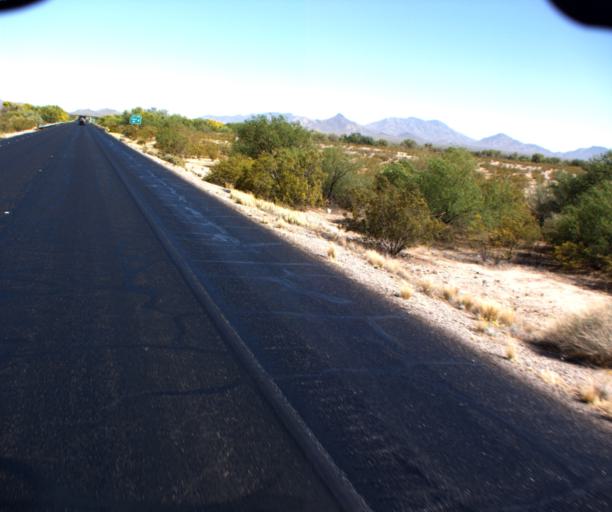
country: US
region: Arizona
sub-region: Pinal County
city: Maricopa
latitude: 32.8427
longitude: -112.2619
